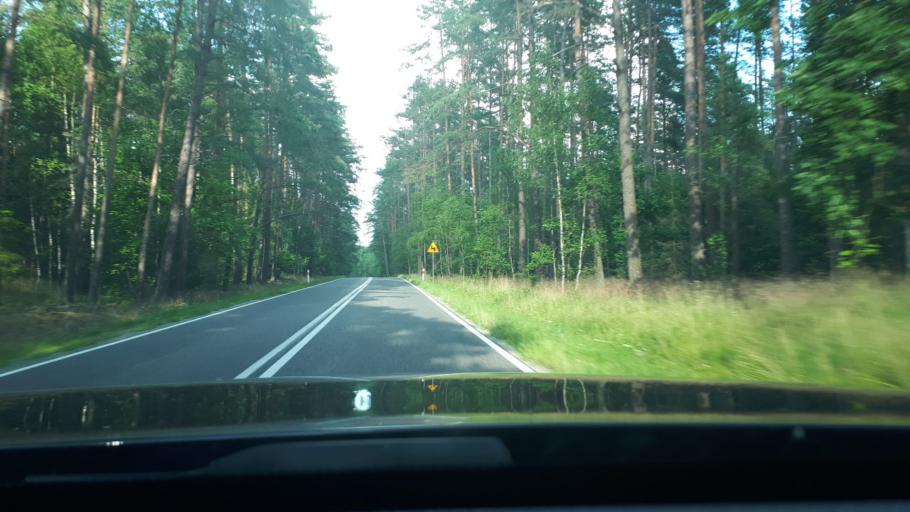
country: PL
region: Warmian-Masurian Voivodeship
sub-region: Powiat olsztynski
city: Stawiguda
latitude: 53.5388
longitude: 20.5367
